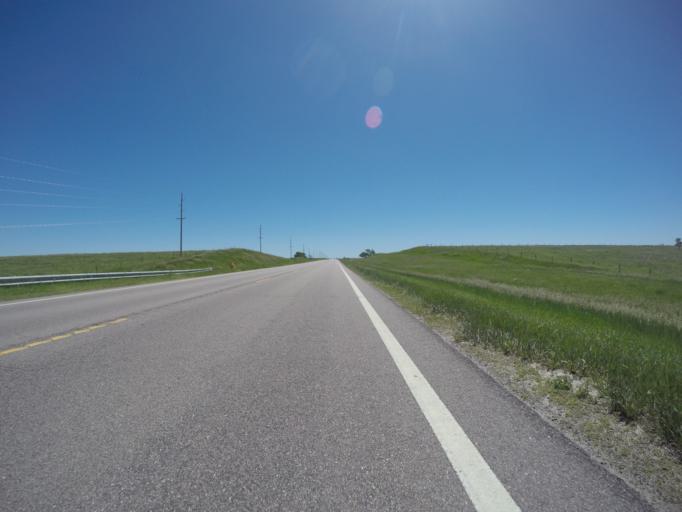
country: US
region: Kansas
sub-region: Norton County
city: Norton
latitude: 39.8284
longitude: -99.6503
